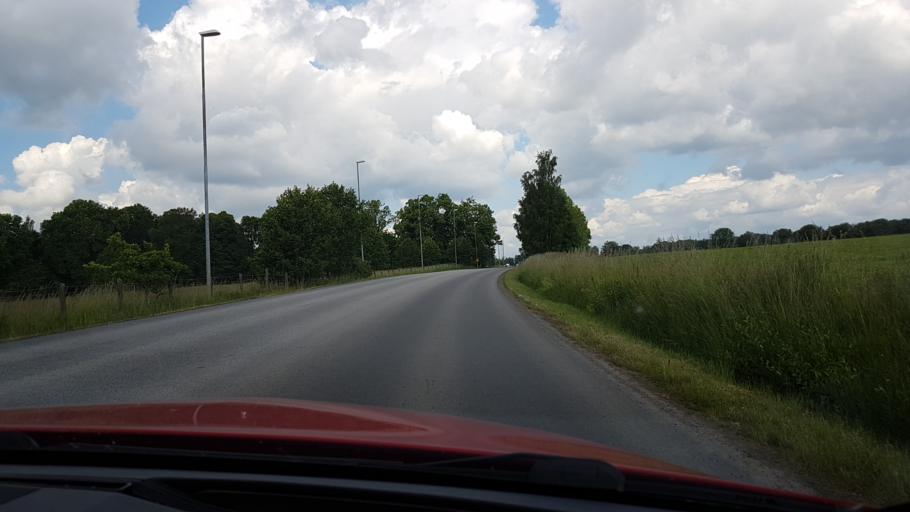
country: SE
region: Vaestra Goetaland
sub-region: Hjo Kommun
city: Hjo
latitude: 58.3144
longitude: 14.2749
